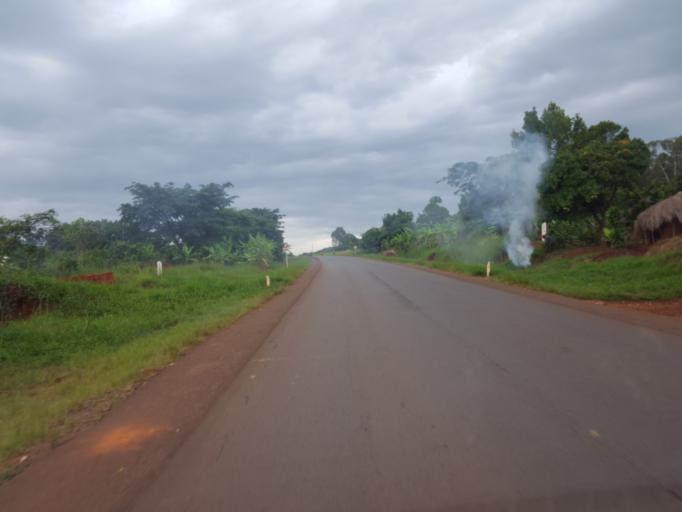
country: UG
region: Central Region
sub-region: Kiboga District
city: Kiboga
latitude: 0.8664
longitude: 31.8577
